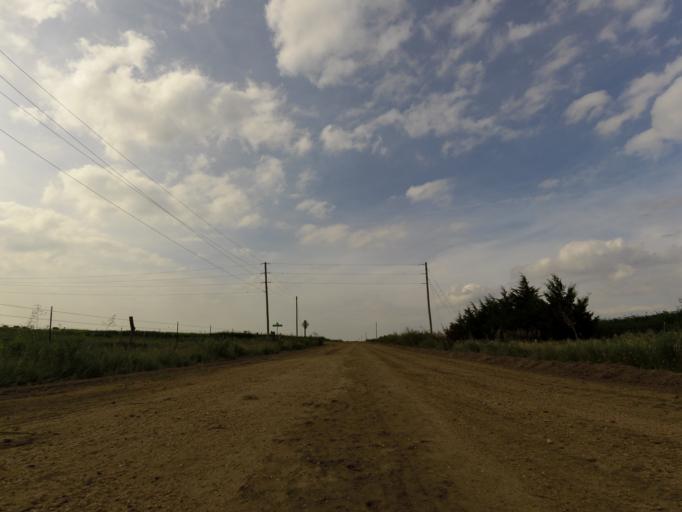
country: US
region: Kansas
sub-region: Reno County
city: South Hutchinson
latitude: 37.9114
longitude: -98.0686
